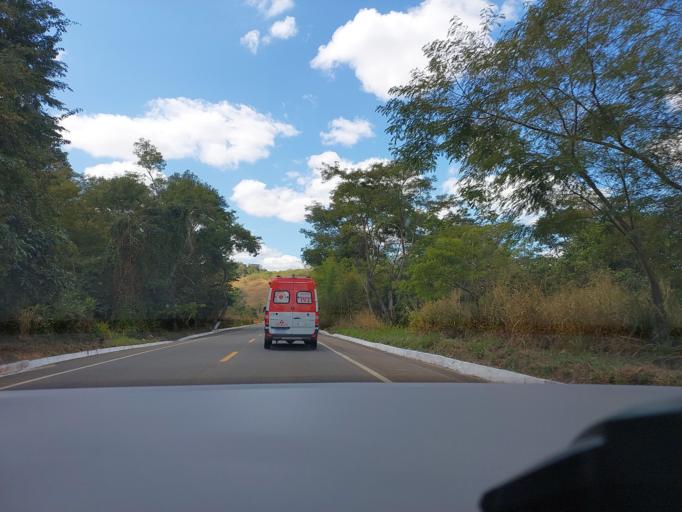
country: BR
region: Minas Gerais
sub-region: Muriae
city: Muriae
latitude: -21.1363
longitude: -42.3000
